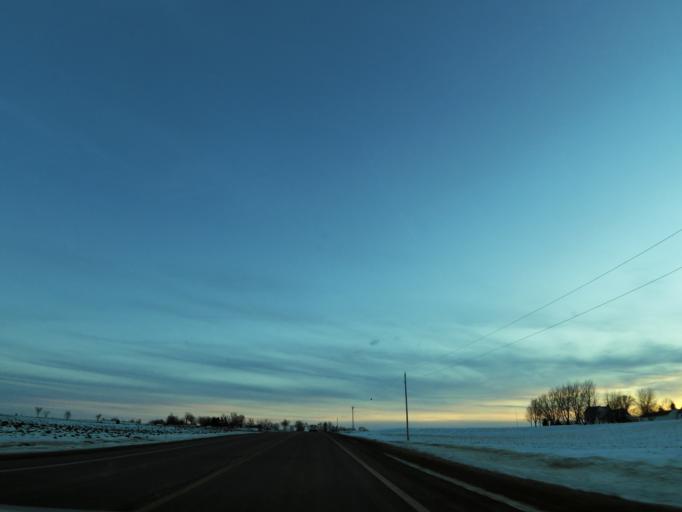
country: US
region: Minnesota
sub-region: Carver County
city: Chaska
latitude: 44.7380
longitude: -93.5622
